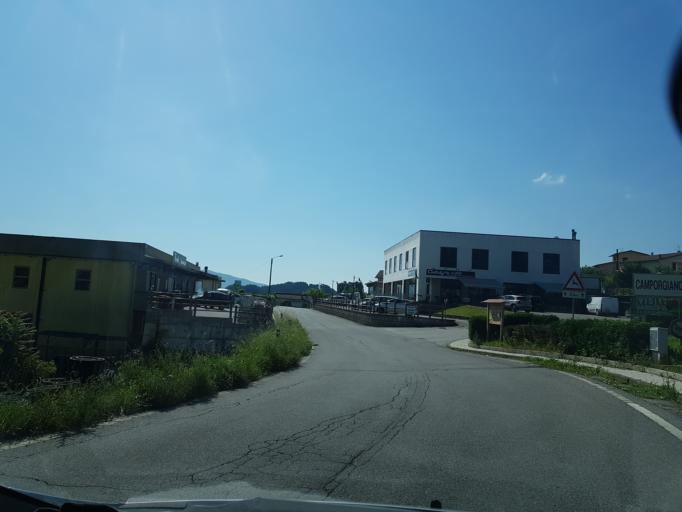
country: IT
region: Tuscany
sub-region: Provincia di Lucca
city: Camporgiano
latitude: 44.1627
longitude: 10.3299
